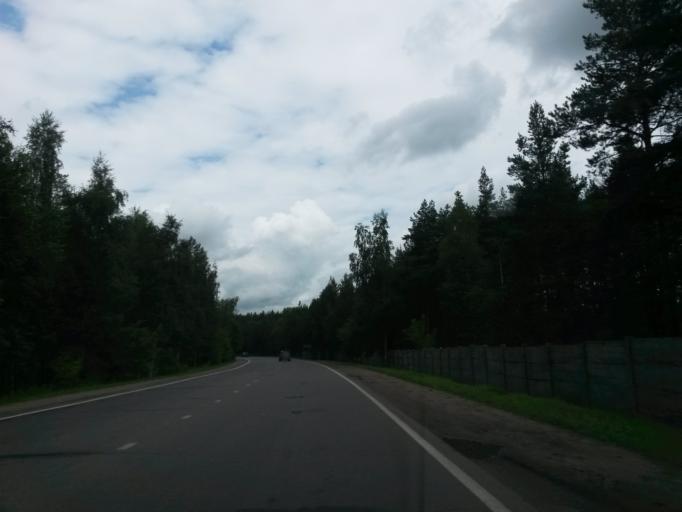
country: RU
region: Jaroslavl
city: Yaroslavl
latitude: 57.6716
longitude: 39.9085
